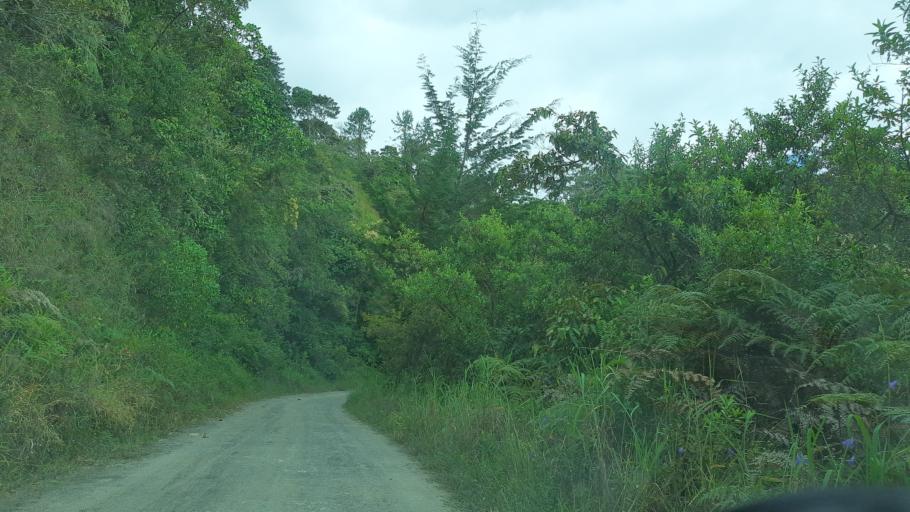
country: CO
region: Boyaca
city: Garagoa
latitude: 5.0321
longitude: -73.3319
